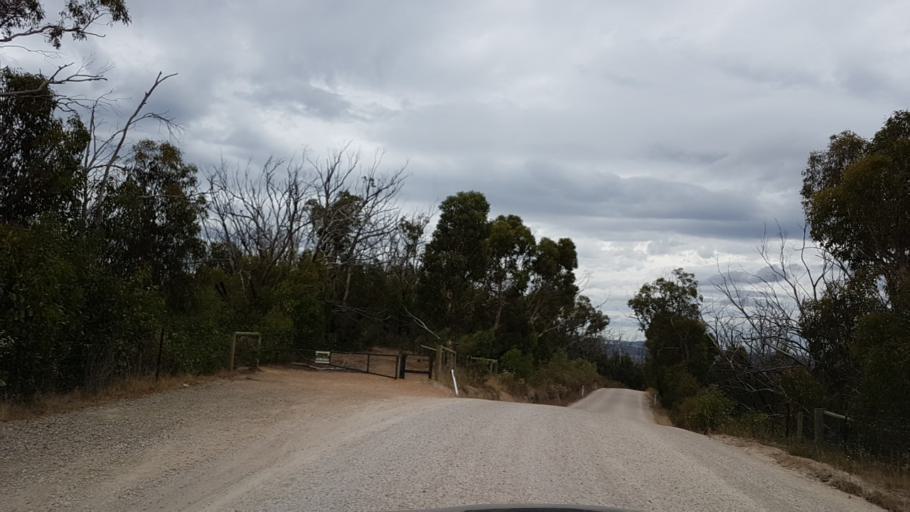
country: AU
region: South Australia
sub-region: Tea Tree Gully
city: Golden Grove
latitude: -34.7743
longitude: 138.8147
